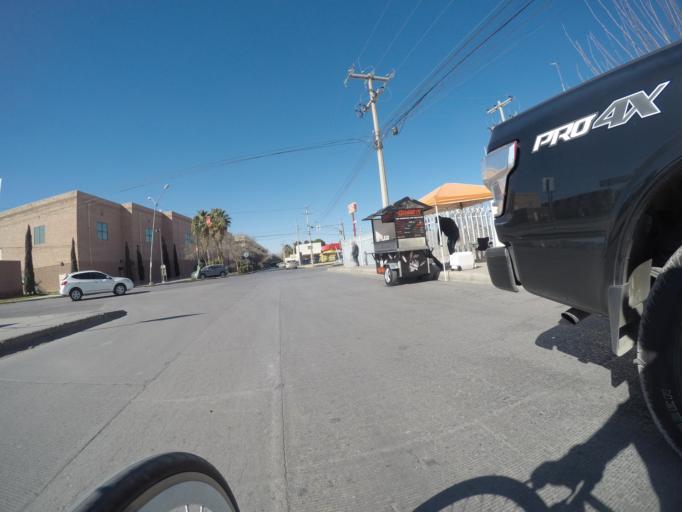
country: MX
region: Chihuahua
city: Ciudad Juarez
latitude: 31.7023
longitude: -106.4134
